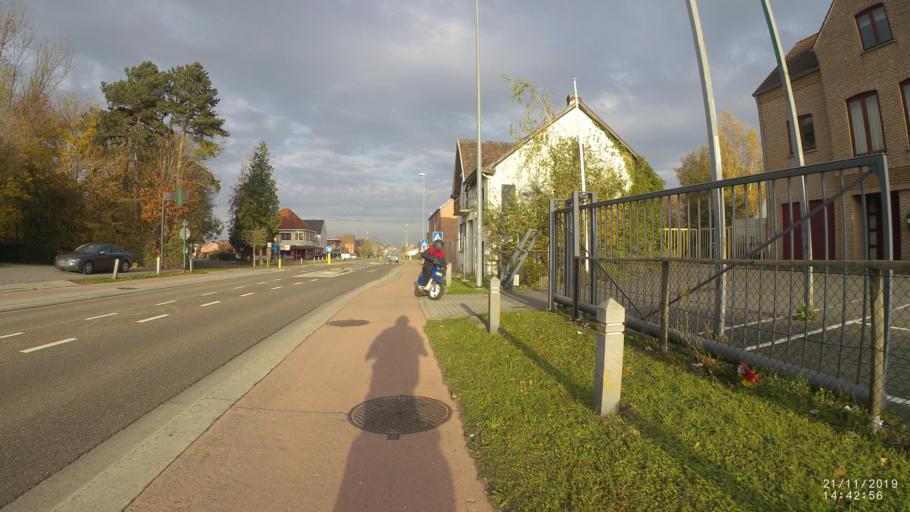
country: BE
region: Flanders
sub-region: Provincie Limburg
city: Alken
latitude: 50.9057
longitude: 5.3150
